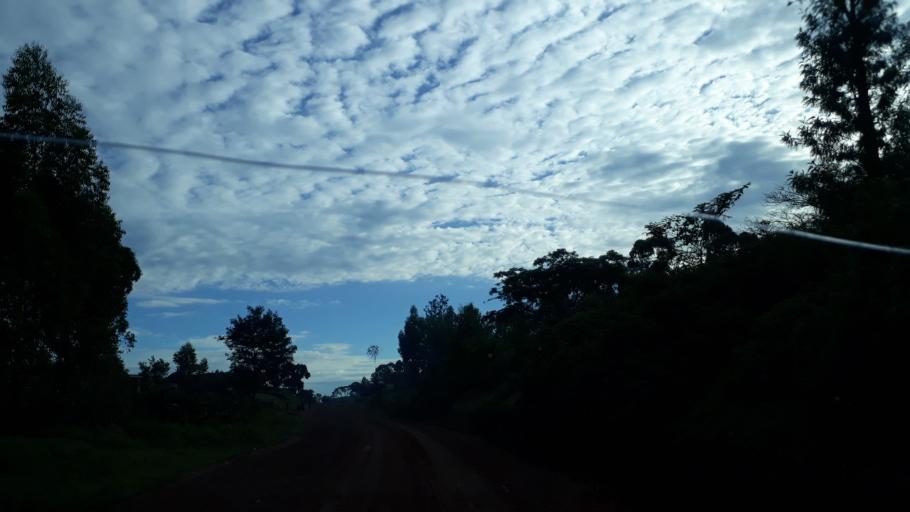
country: UG
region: Northern Region
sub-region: Zombo District
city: Paidha
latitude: 2.2325
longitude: 30.8581
